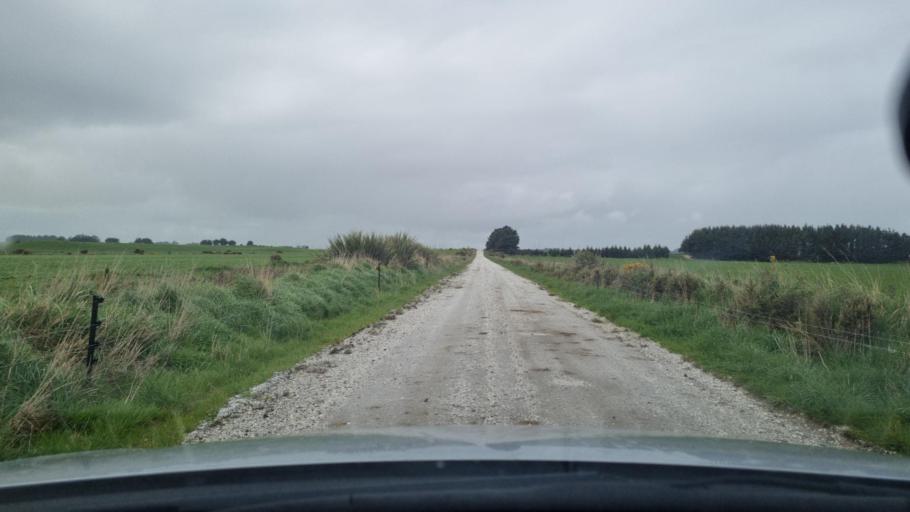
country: NZ
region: Southland
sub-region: Invercargill City
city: Invercargill
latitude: -46.5032
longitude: 168.4029
